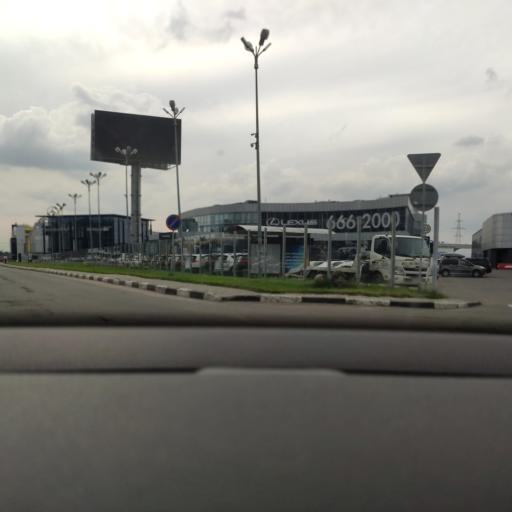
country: RU
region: Moskovskaya
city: Reutov
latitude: 55.7849
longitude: 37.8736
